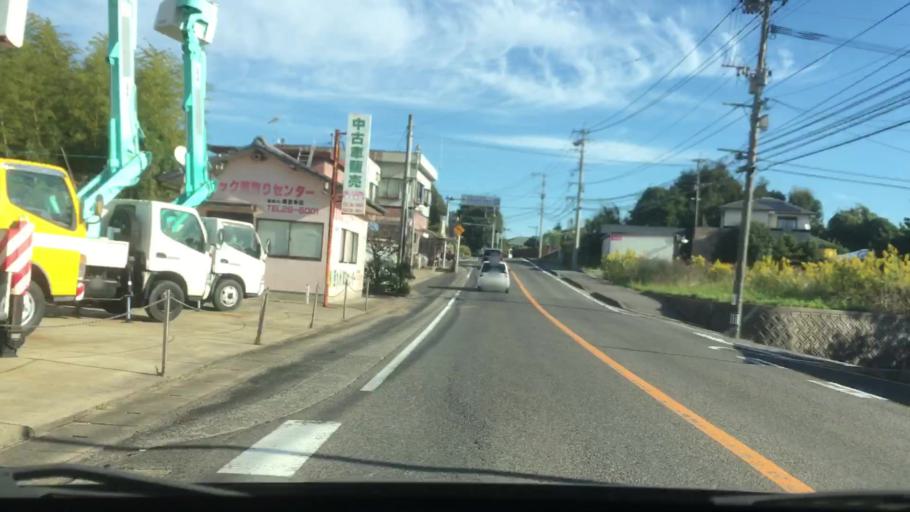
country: JP
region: Nagasaki
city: Sasebo
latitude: 33.0614
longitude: 129.7636
